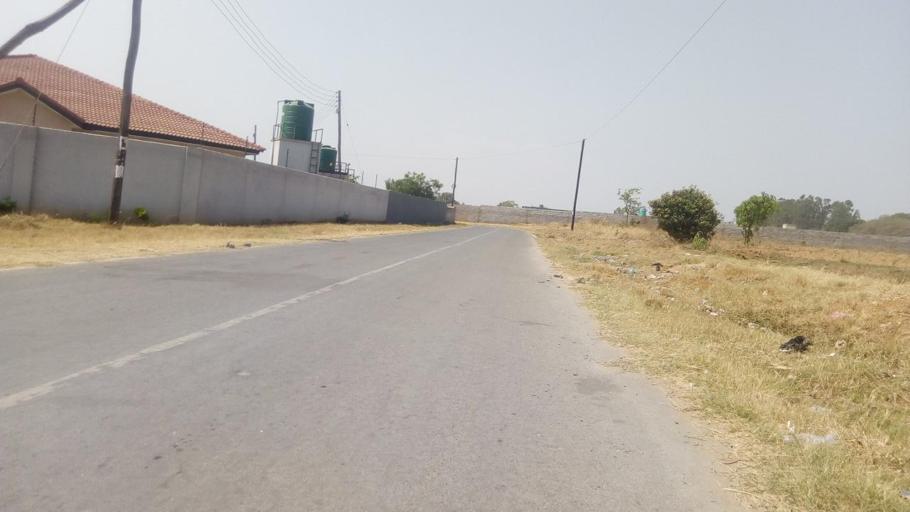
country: ZM
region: Lusaka
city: Lusaka
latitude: -15.3616
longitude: 28.2843
